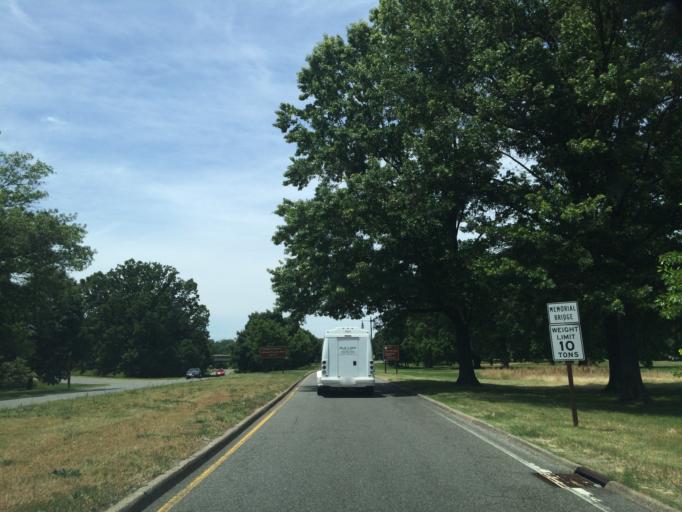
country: US
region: Washington, D.C.
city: Washington, D.C.
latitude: 38.8818
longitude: -77.0550
